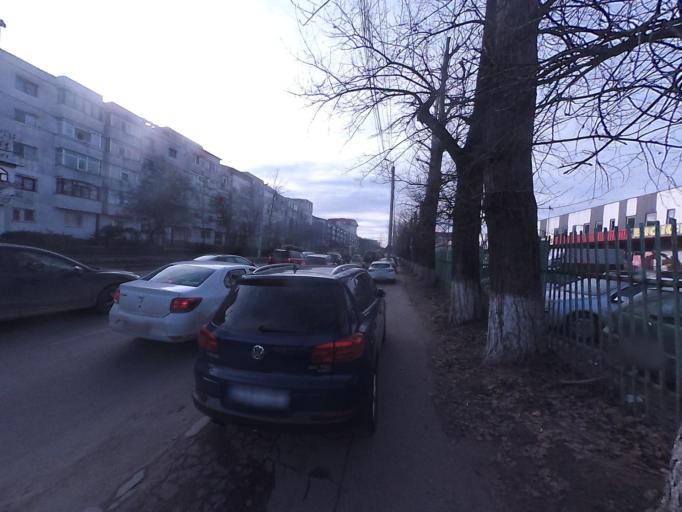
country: RO
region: Iasi
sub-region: Municipiul Iasi
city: Iasi
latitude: 47.1360
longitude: 27.5905
